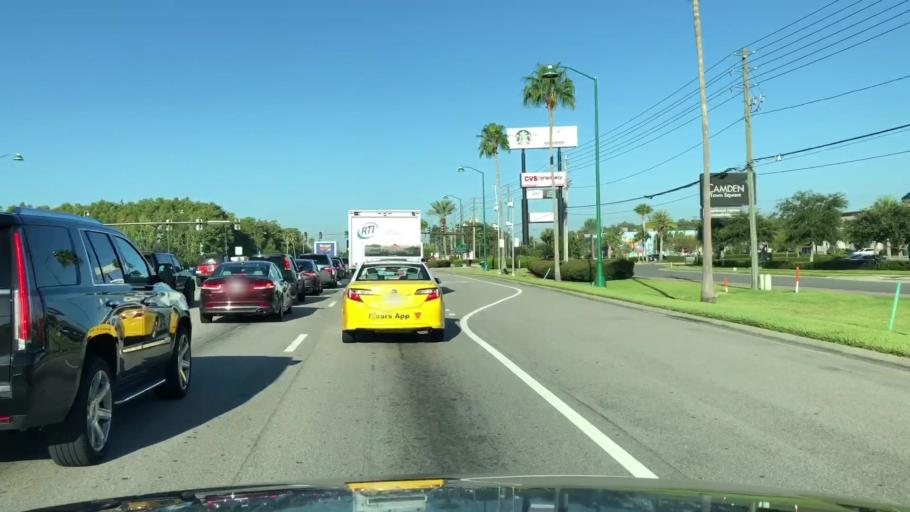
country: US
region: Florida
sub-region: Osceola County
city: Celebration
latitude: 28.3329
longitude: -81.5267
